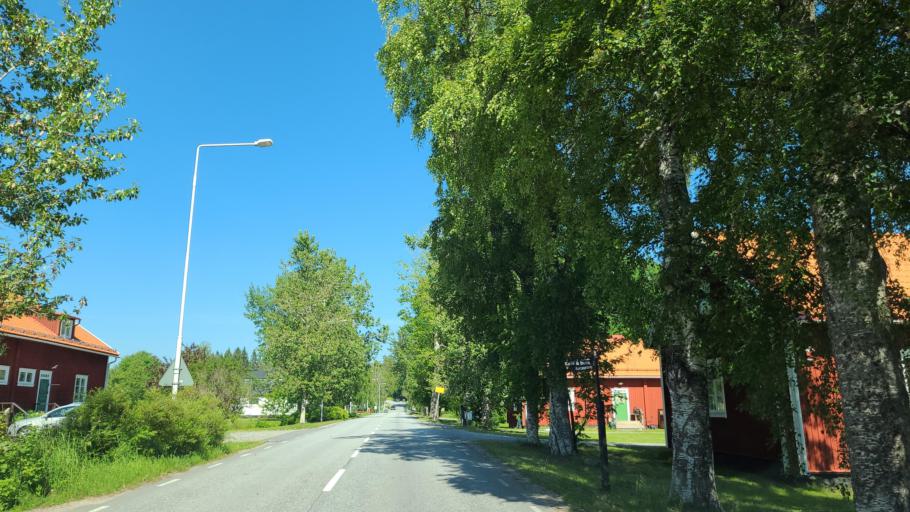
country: SE
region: Vaesterbotten
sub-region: Nordmalings Kommun
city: Nordmaling
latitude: 63.5806
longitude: 19.4418
